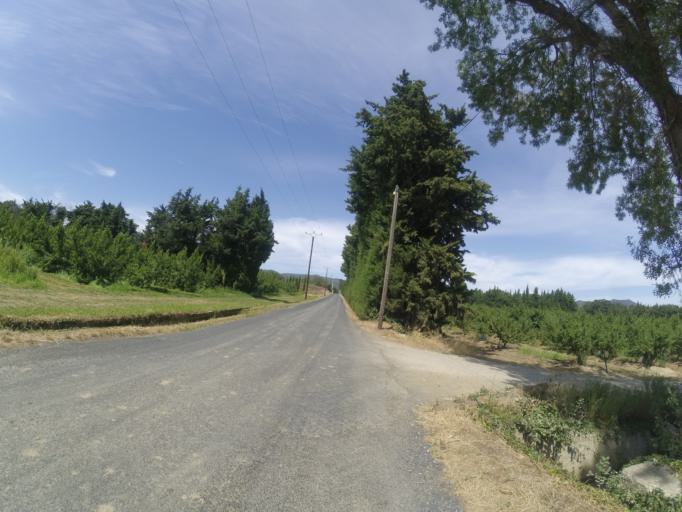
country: FR
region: Languedoc-Roussillon
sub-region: Departement des Pyrenees-Orientales
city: Millas
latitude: 42.6788
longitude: 2.6694
